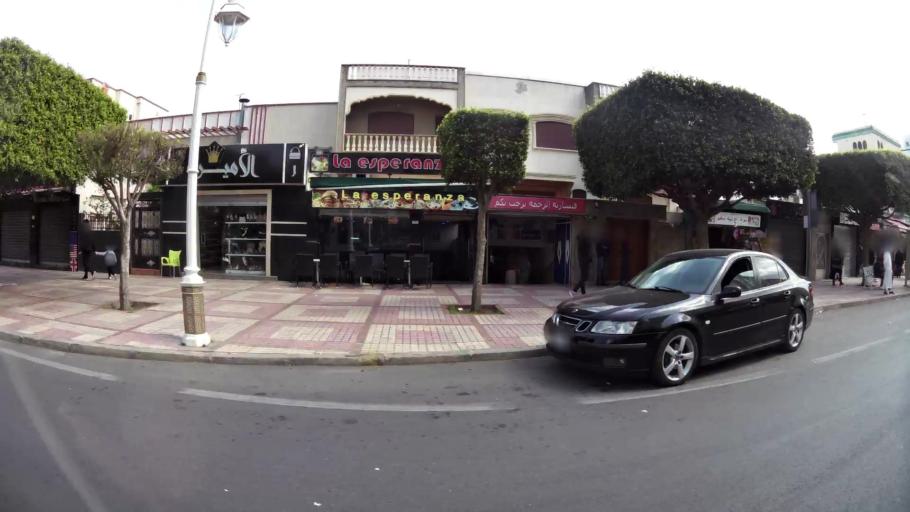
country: MA
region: Tanger-Tetouan
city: Tetouan
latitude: 35.5826
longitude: -5.3511
